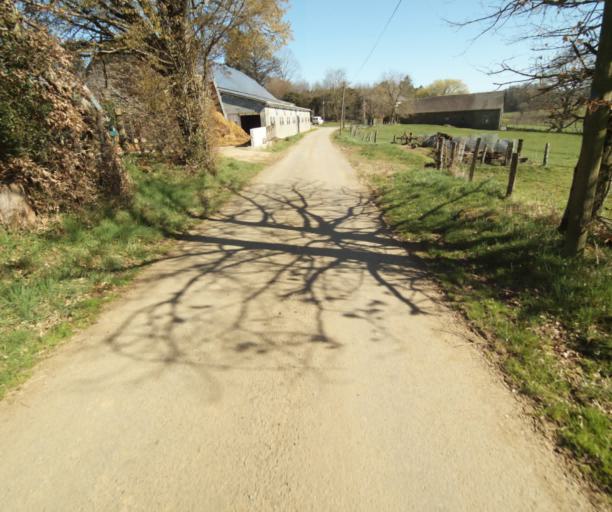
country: FR
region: Limousin
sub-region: Departement de la Correze
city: Chamboulive
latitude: 45.4153
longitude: 1.6741
